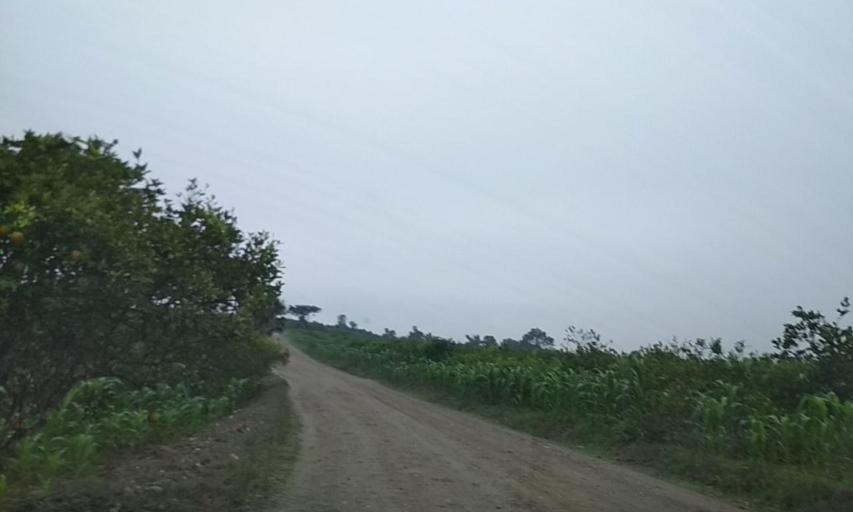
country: MX
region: Veracruz
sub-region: Papantla
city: El Chote
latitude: 20.3359
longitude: -97.3905
